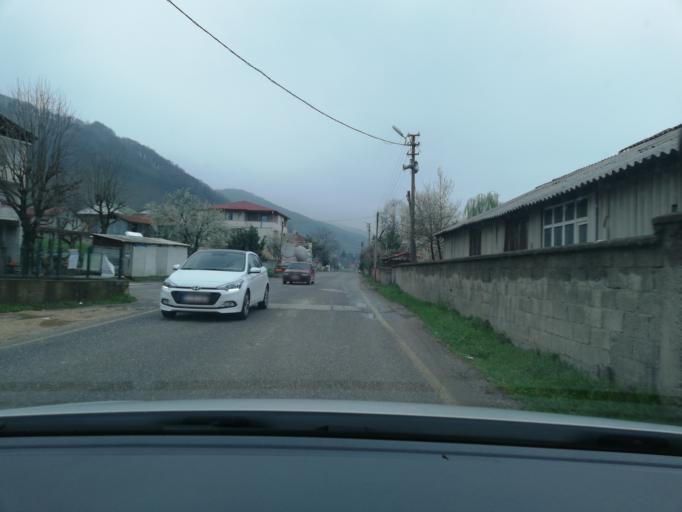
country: TR
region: Duzce
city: Kaynasli
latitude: 40.7736
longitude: 31.3347
